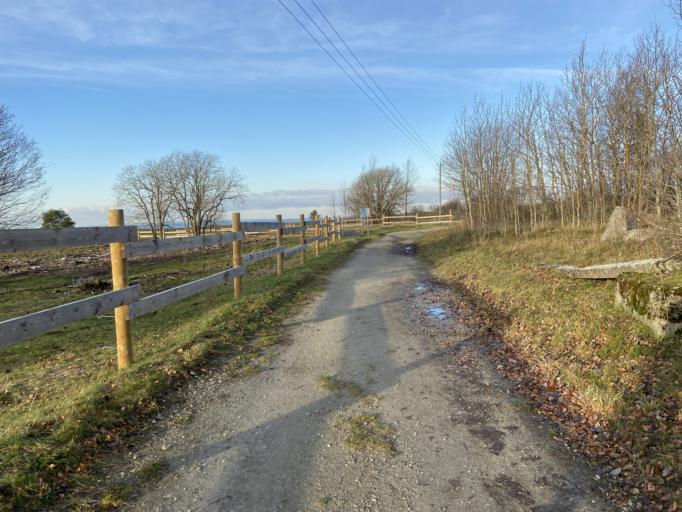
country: EE
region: Harju
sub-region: Tallinna linn
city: Tallinn
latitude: 59.4821
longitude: 24.7098
